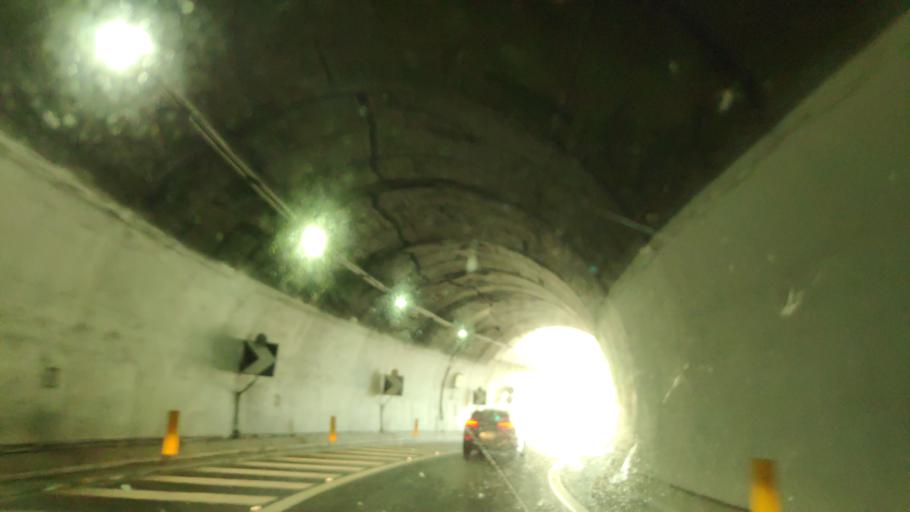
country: IT
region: Campania
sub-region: Provincia di Napoli
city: Napoli
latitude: 40.8606
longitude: 14.2327
